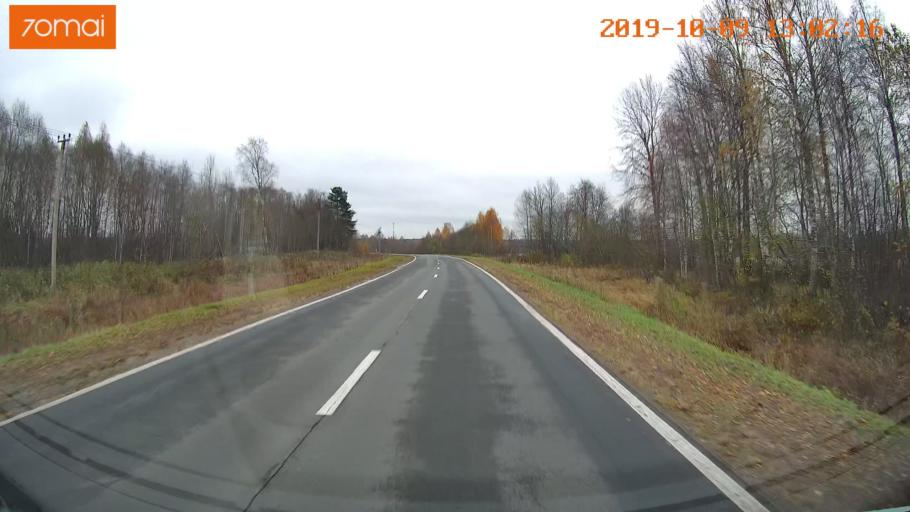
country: RU
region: Jaroslavl
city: Prechistoye
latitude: 58.3626
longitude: 40.4977
